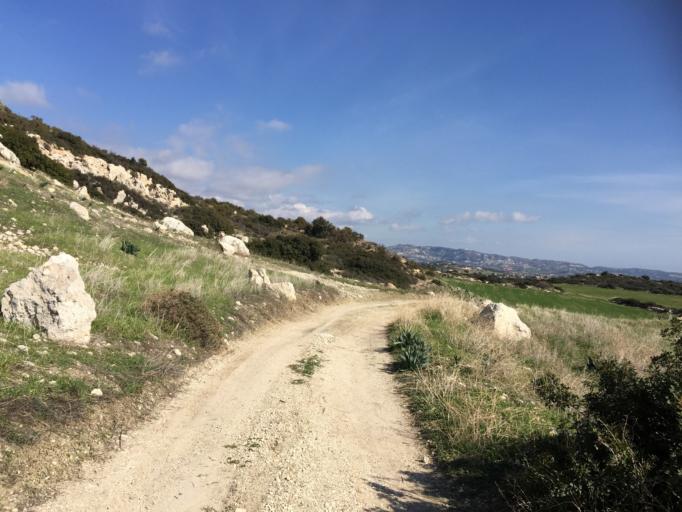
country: CY
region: Larnaka
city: Agios Tychon
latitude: 34.7366
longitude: 33.1378
